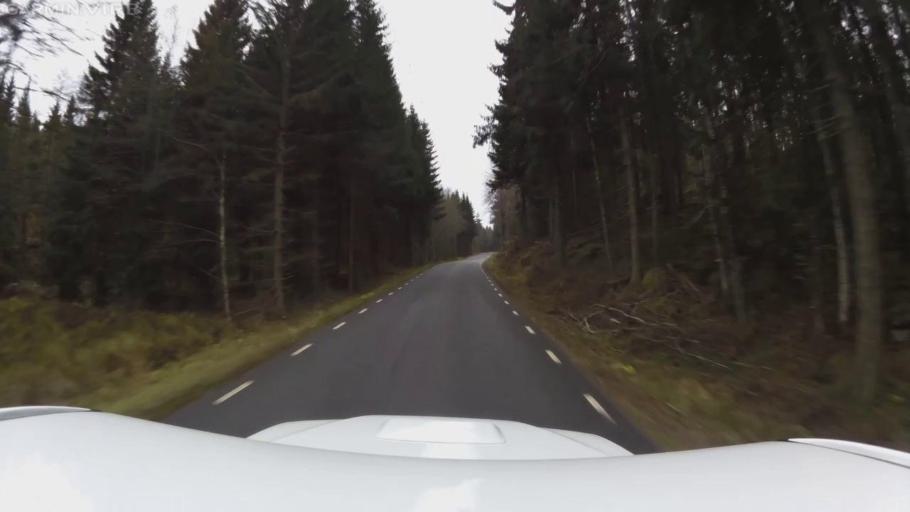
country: SE
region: OEstergoetland
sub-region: Mjolby Kommun
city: Mantorp
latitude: 58.1729
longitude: 15.3978
